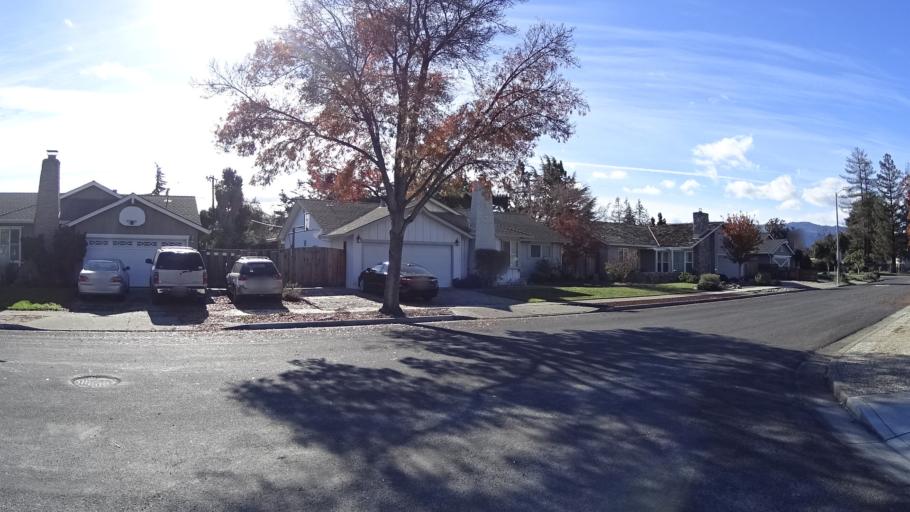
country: US
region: California
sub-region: Santa Clara County
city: Sunnyvale
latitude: 37.3507
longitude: -122.0406
